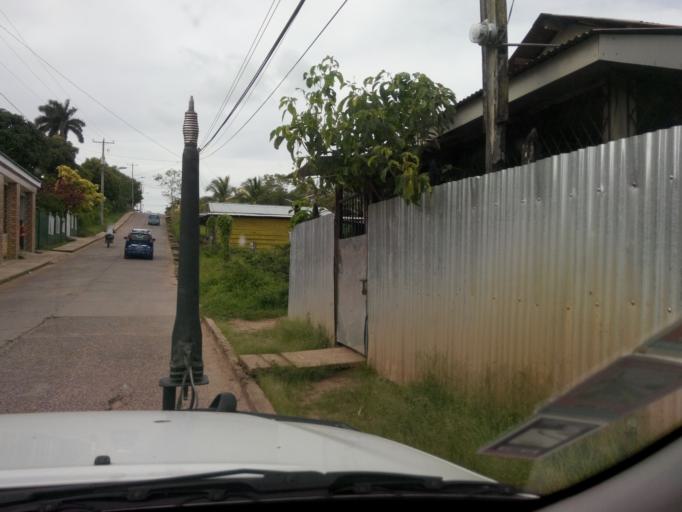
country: NI
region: Atlantico Sur
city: Bluefields
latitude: 12.0283
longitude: -83.7681
